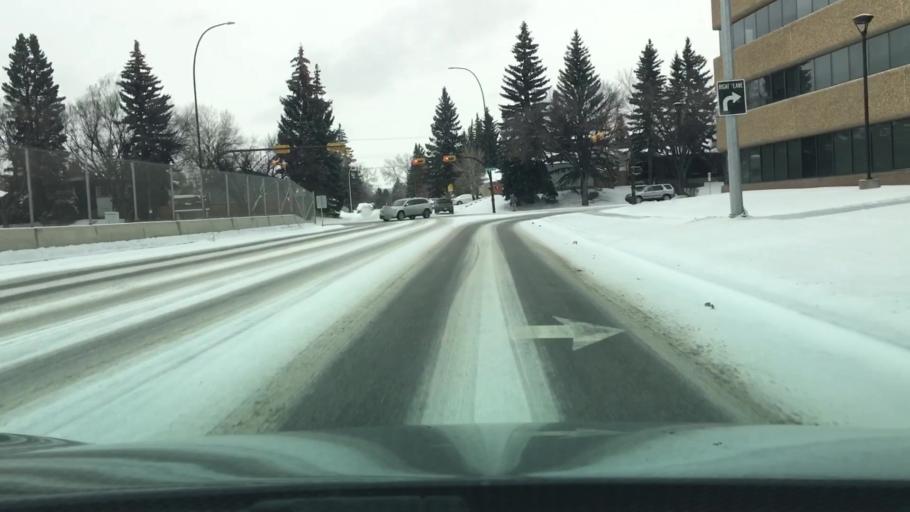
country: CA
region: Alberta
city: Calgary
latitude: 51.0876
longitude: -114.1585
